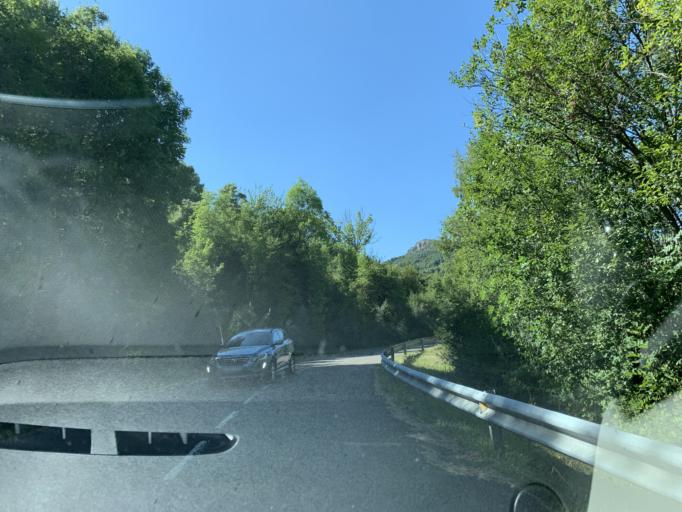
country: ES
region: Aragon
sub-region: Provincia de Huesca
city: Hoz de Jaca
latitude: 42.7029
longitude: -0.3236
